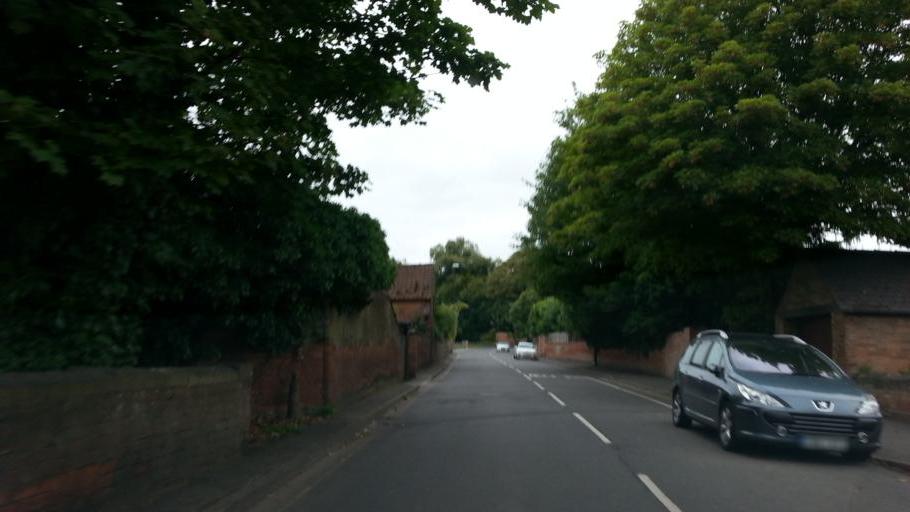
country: GB
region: England
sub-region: Nottinghamshire
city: Southwell
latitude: 53.0763
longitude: -0.9497
